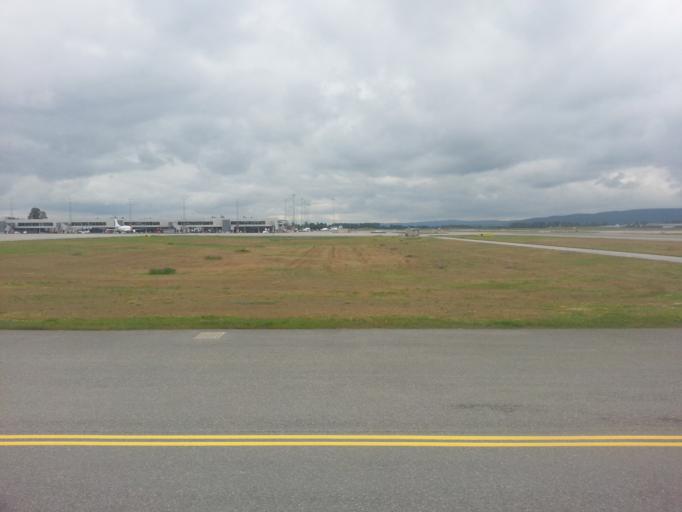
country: NO
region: Akershus
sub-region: Nannestad
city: Teigebyen
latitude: 60.1976
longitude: 11.0884
